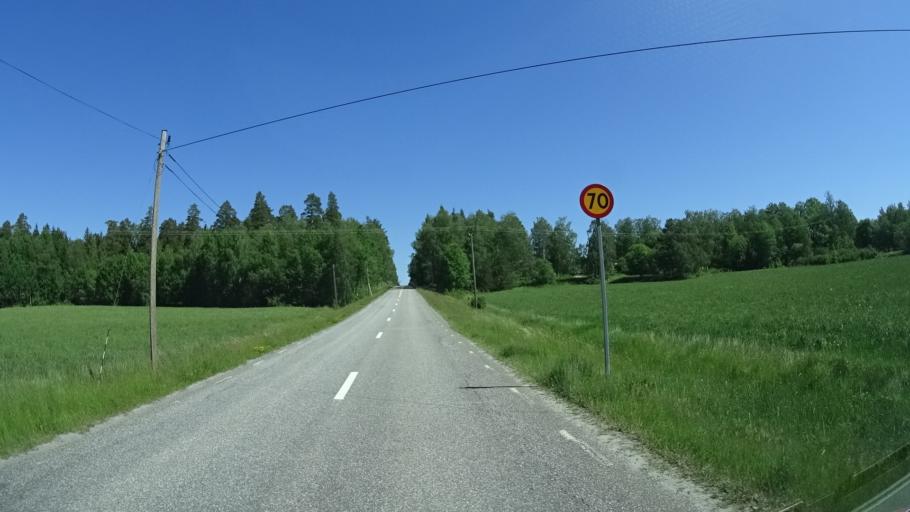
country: SE
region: Stockholm
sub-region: Vallentuna Kommun
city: Vallentuna
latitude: 59.6051
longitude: 18.1396
